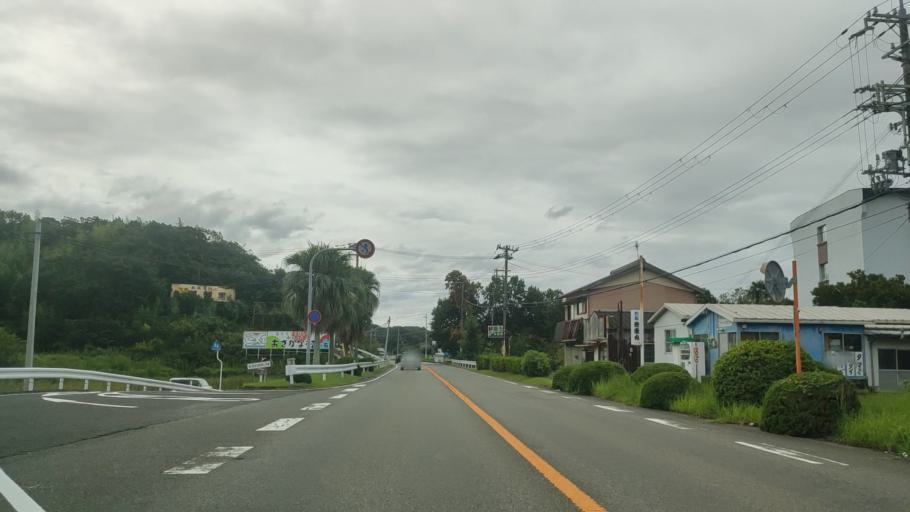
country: JP
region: Wakayama
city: Tanabe
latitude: 33.6985
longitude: 135.3885
